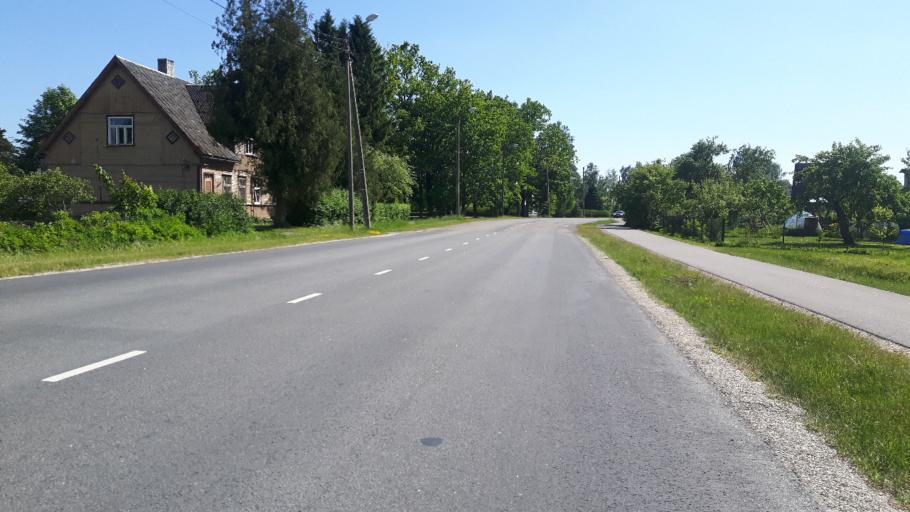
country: EE
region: Paernumaa
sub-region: Sindi linn
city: Sindi
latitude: 58.4010
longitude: 24.6462
